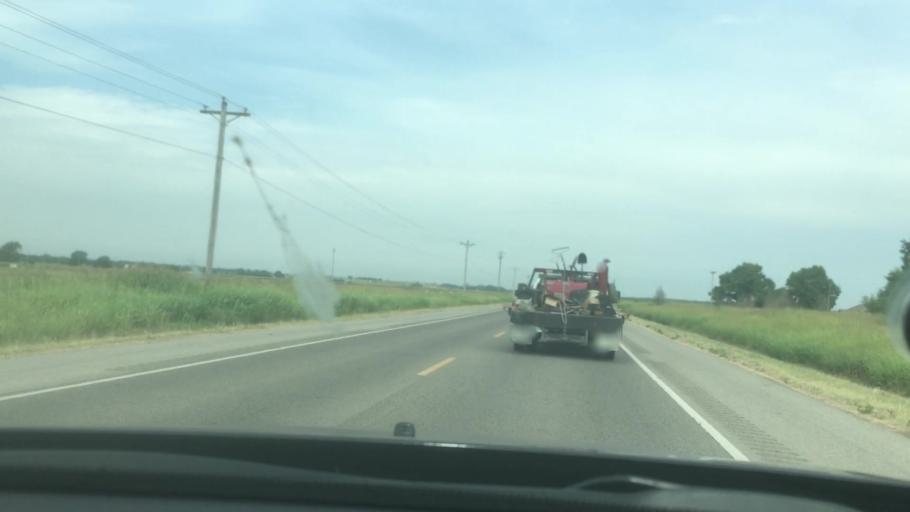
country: US
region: Oklahoma
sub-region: Garvin County
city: Lindsay
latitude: 34.8228
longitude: -97.5255
